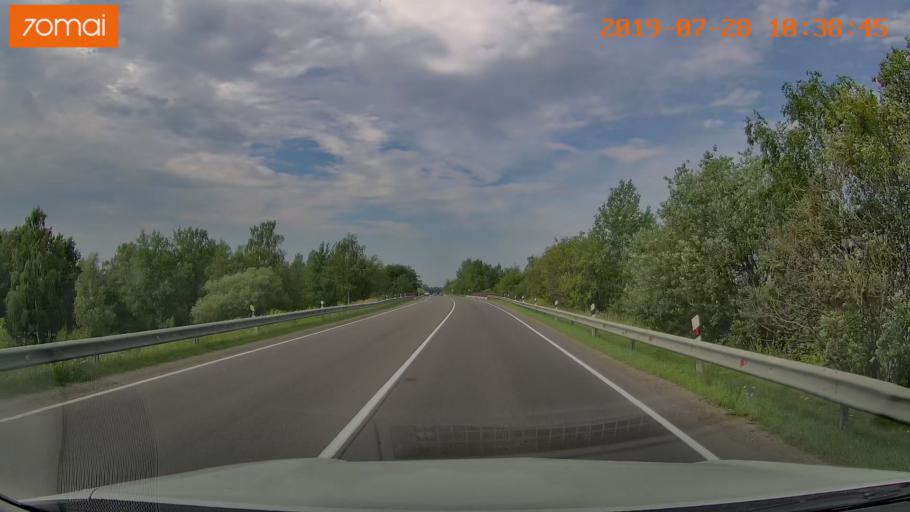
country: RU
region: Kaliningrad
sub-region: Gorod Kaliningrad
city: Kaliningrad
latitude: 54.7221
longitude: 20.3934
